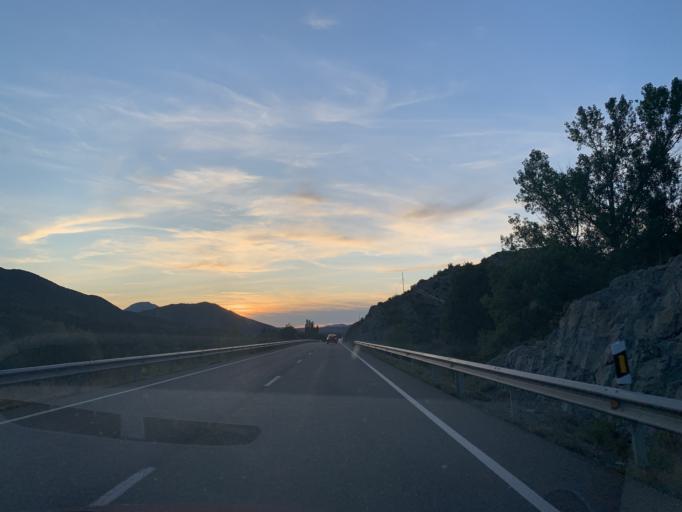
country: ES
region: Aragon
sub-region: Provincia de Huesca
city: Yebra de Basa
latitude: 42.4919
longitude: -0.3212
